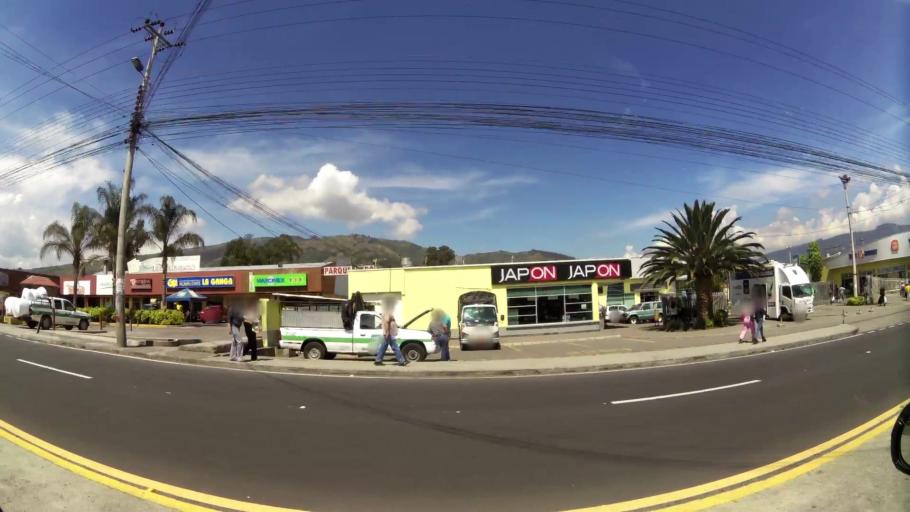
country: EC
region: Pichincha
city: Quito
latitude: -0.2152
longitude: -78.4057
